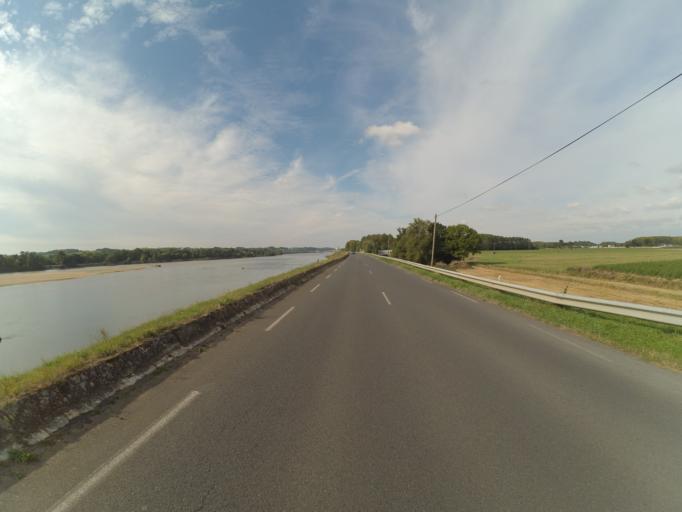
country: FR
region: Pays de la Loire
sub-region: Departement de Maine-et-Loire
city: Villebernier
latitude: 47.2482
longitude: -0.0073
